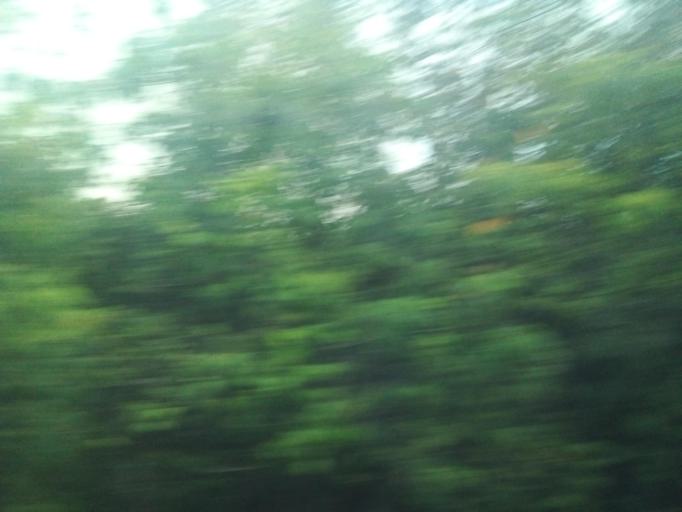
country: BR
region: Maranhao
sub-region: Imperatriz
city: Imperatriz
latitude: -4.9273
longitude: -47.4261
